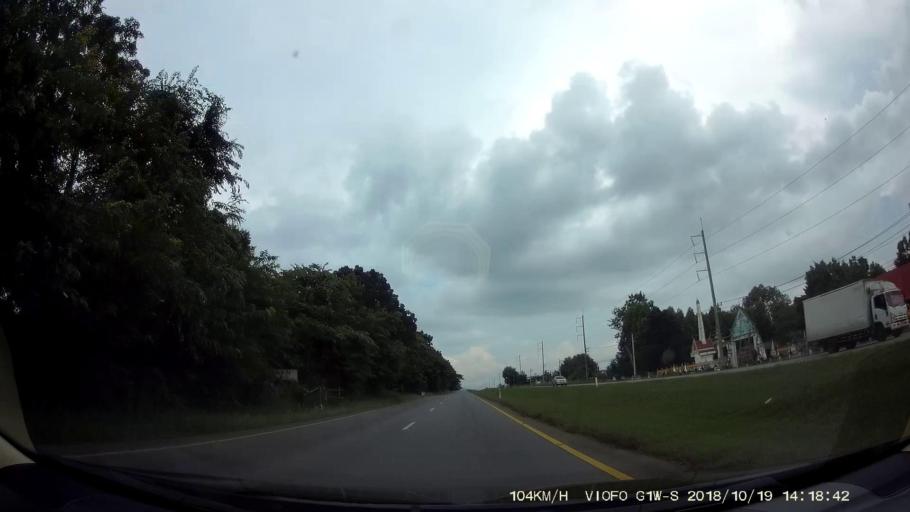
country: TH
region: Chaiyaphum
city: Kaeng Khro
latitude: 16.0188
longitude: 102.2378
